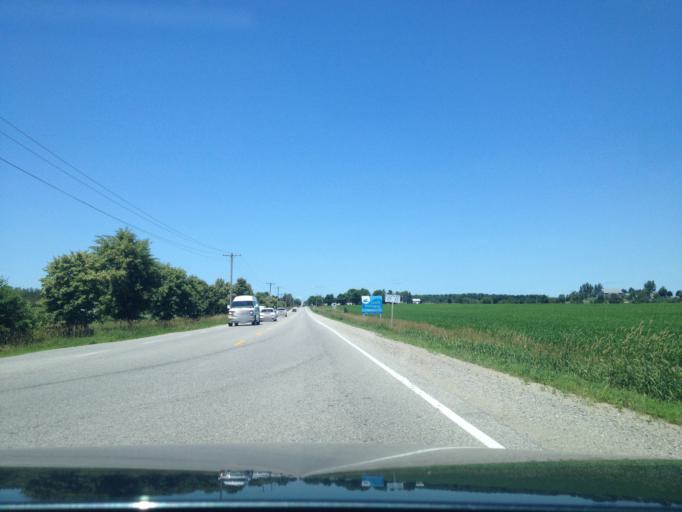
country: CA
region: Ontario
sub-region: Wellington County
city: Guelph
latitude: 43.6631
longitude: -80.2811
